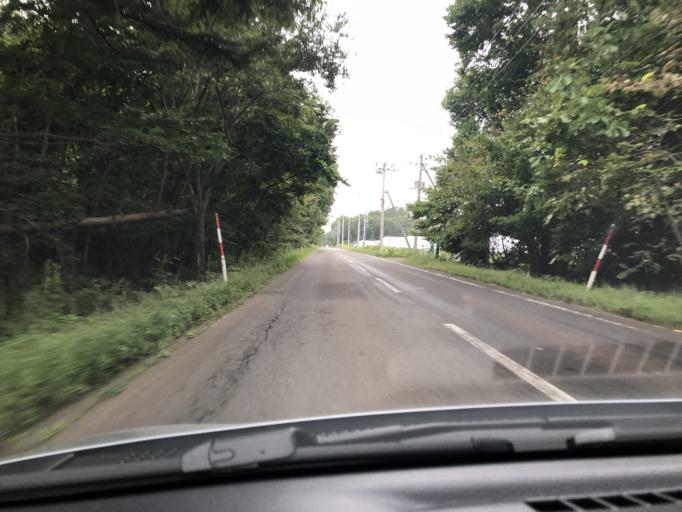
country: JP
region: Hokkaido
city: Chitose
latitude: 42.8714
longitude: 141.7279
